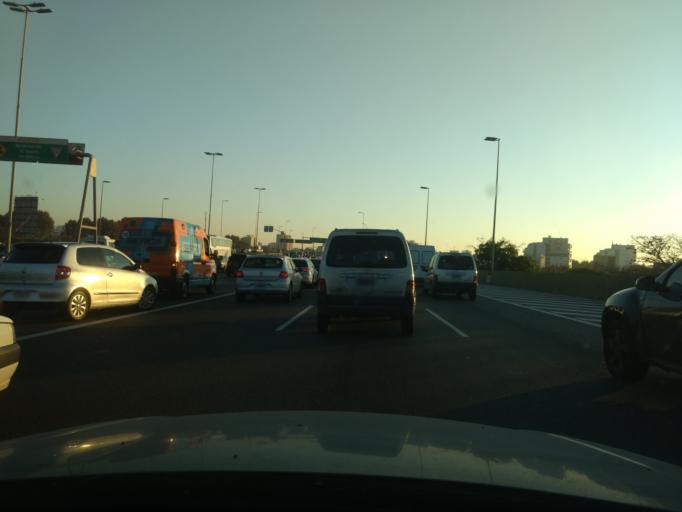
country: AR
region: Buenos Aires F.D.
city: Villa Lugano
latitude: -34.6455
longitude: -58.4625
